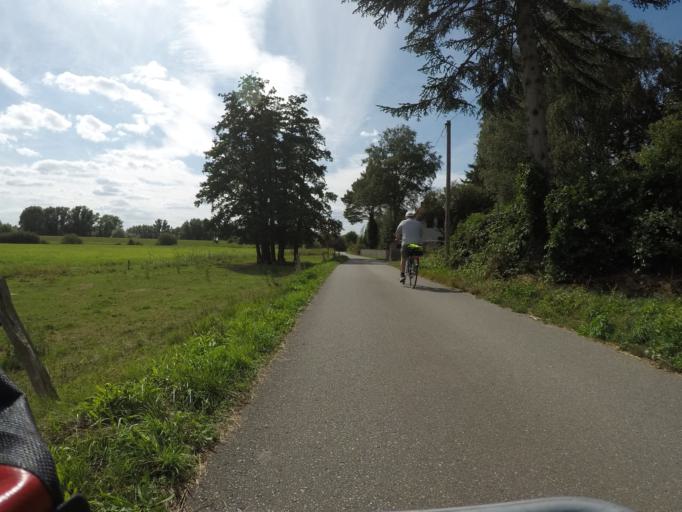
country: DE
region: Lower Saxony
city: Radbruch
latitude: 53.3659
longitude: 10.2844
